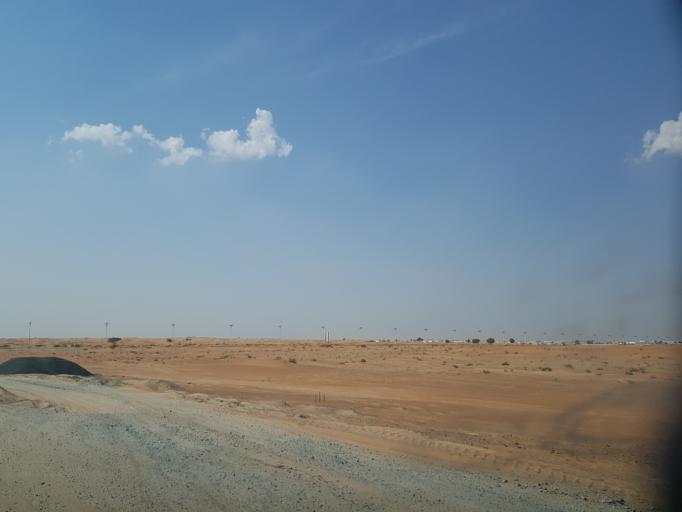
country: AE
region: Ash Shariqah
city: Adh Dhayd
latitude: 25.2557
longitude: 55.7354
